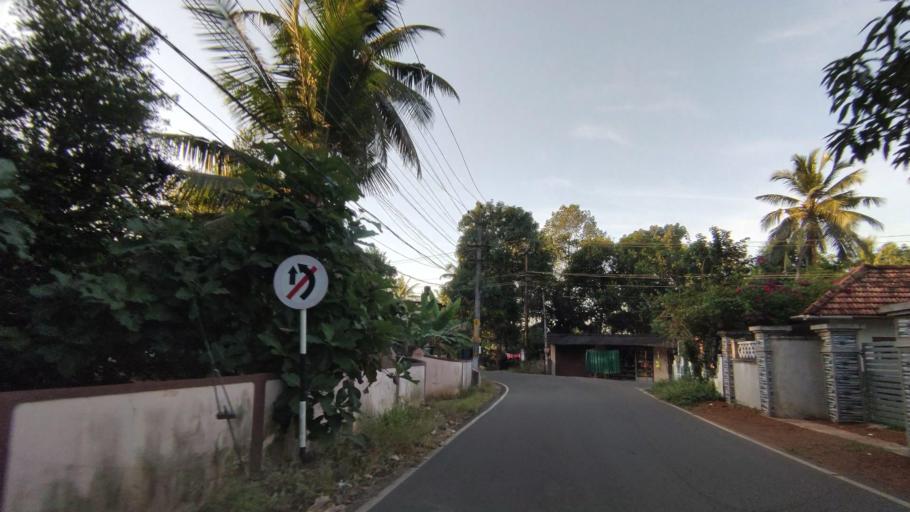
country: IN
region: Kerala
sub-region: Kottayam
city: Kottayam
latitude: 9.6210
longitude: 76.4939
